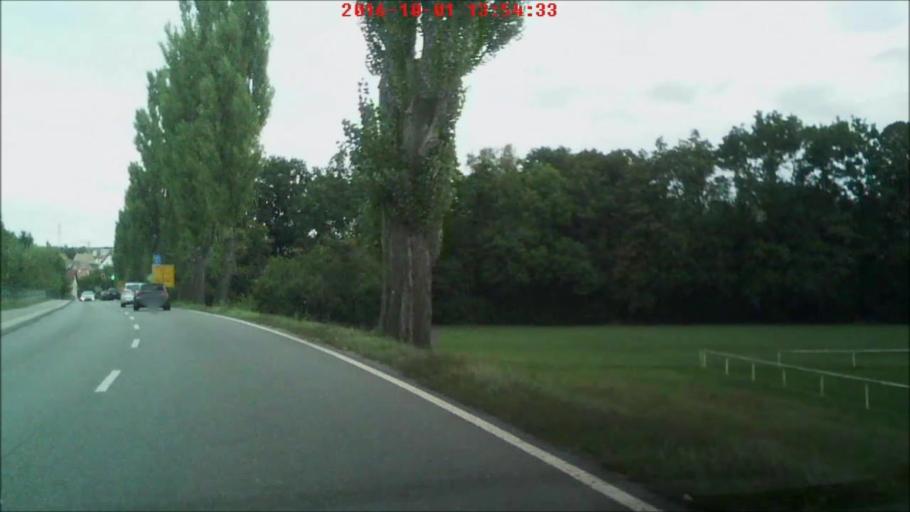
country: DE
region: Thuringia
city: Mellingen
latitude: 50.9365
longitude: 11.3931
